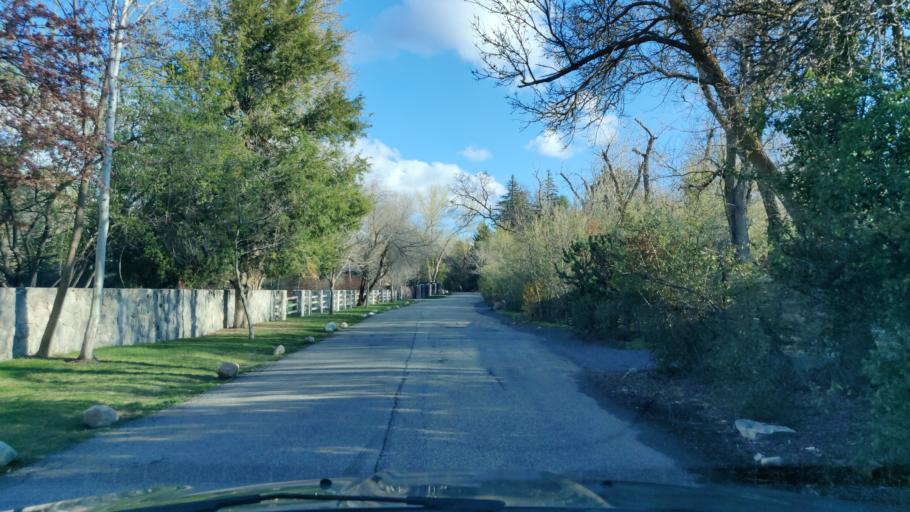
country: US
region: Utah
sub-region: Salt Lake County
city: Cottonwood Heights
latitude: 40.6434
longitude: -111.8199
